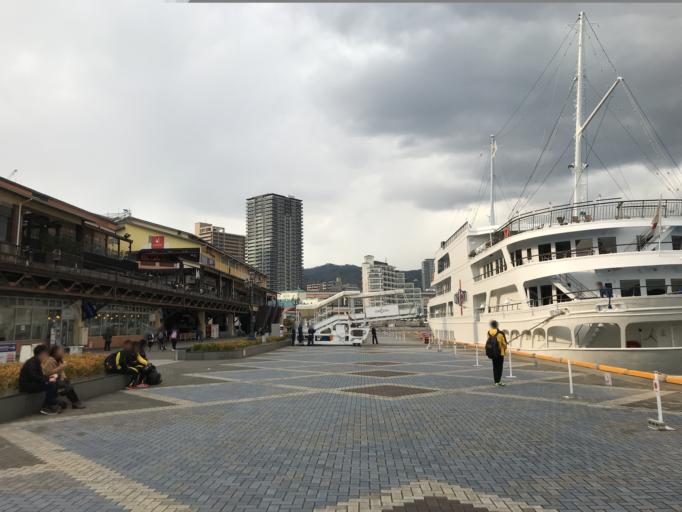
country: JP
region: Hyogo
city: Kobe
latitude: 34.6793
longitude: 135.1854
